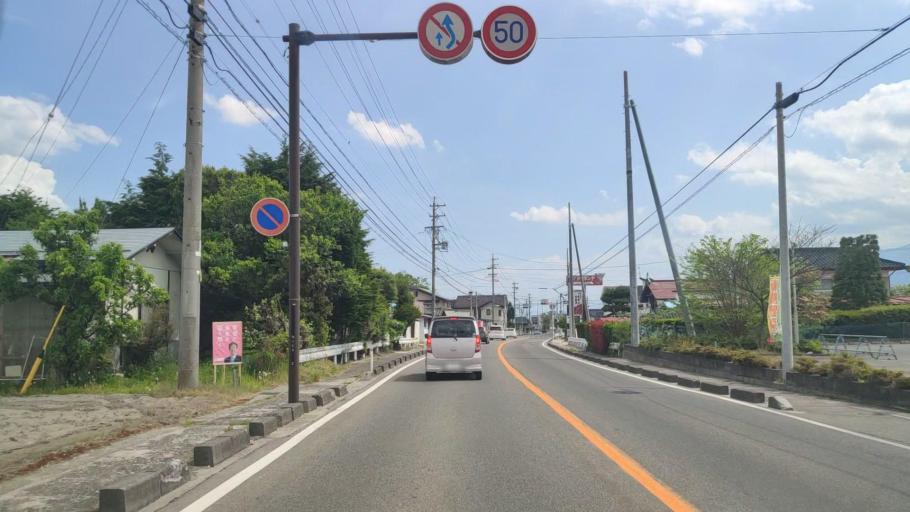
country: JP
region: Nagano
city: Omachi
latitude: 36.4672
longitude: 137.8494
